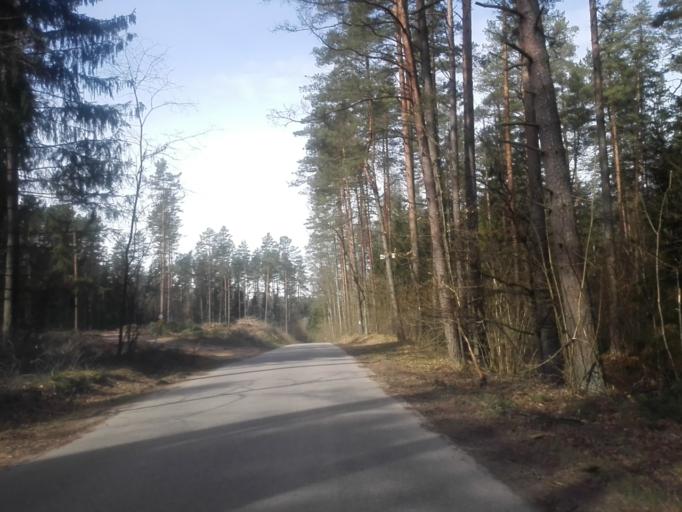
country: PL
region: Podlasie
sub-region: Powiat sejnenski
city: Sejny
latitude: 54.0320
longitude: 23.3700
